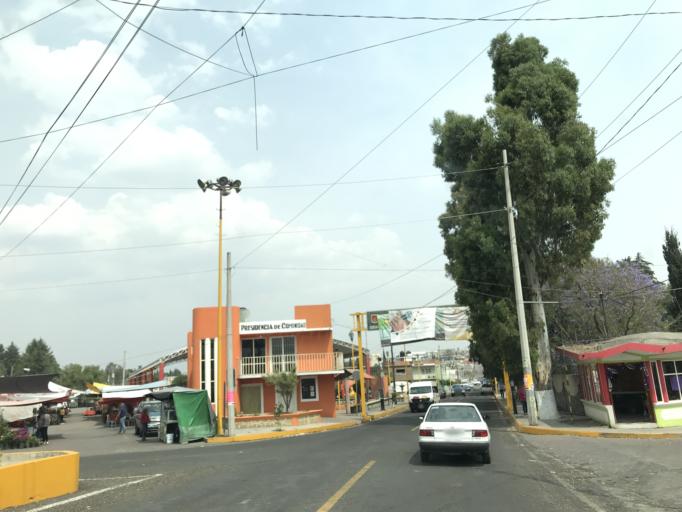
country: MX
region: Tlaxcala
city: Panotla
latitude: 19.3191
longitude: -98.2723
